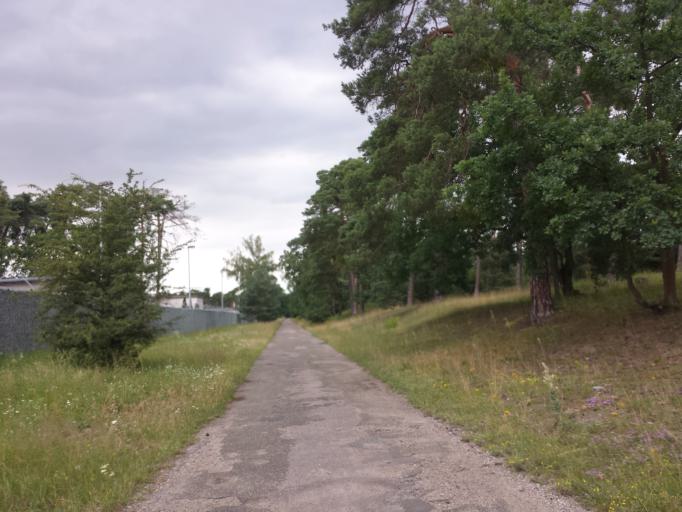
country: DE
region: Hesse
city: Viernheim
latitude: 49.5237
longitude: 8.5382
